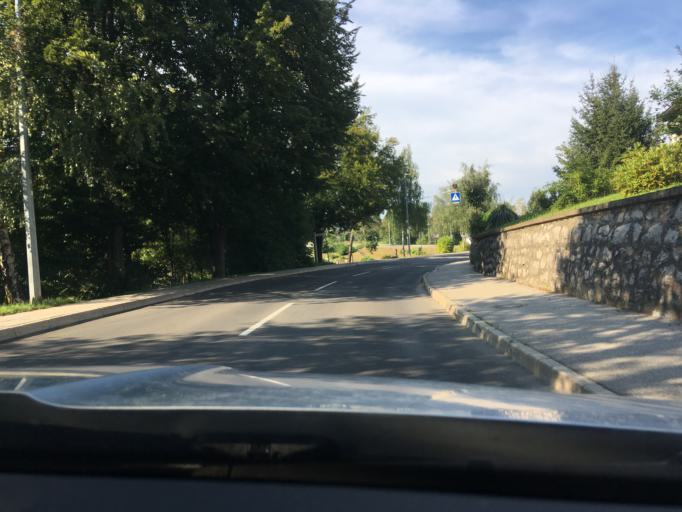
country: SI
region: Crnomelj
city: Crnomelj
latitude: 45.5773
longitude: 15.1901
